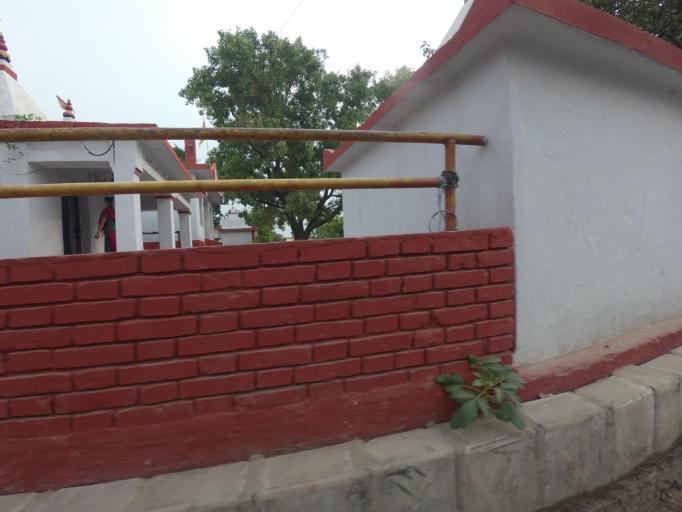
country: NP
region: Western Region
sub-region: Lumbini Zone
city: Bhairahawa
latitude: 27.5201
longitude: 83.4425
